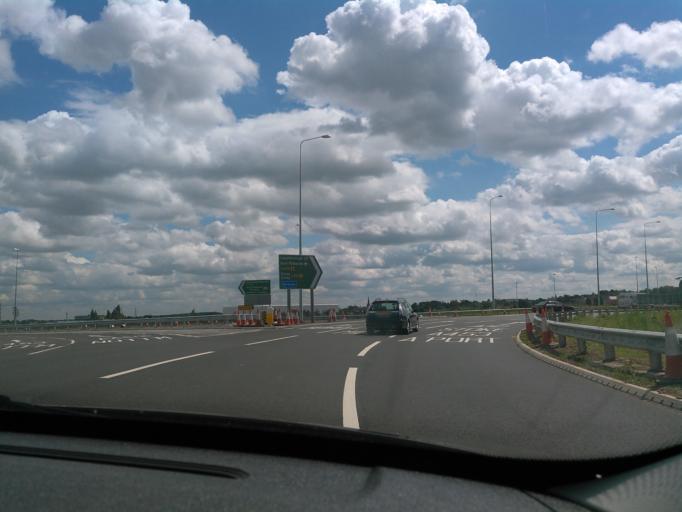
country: GB
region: England
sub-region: Leicestershire
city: Kegworth
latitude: 52.8449
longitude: -1.2946
